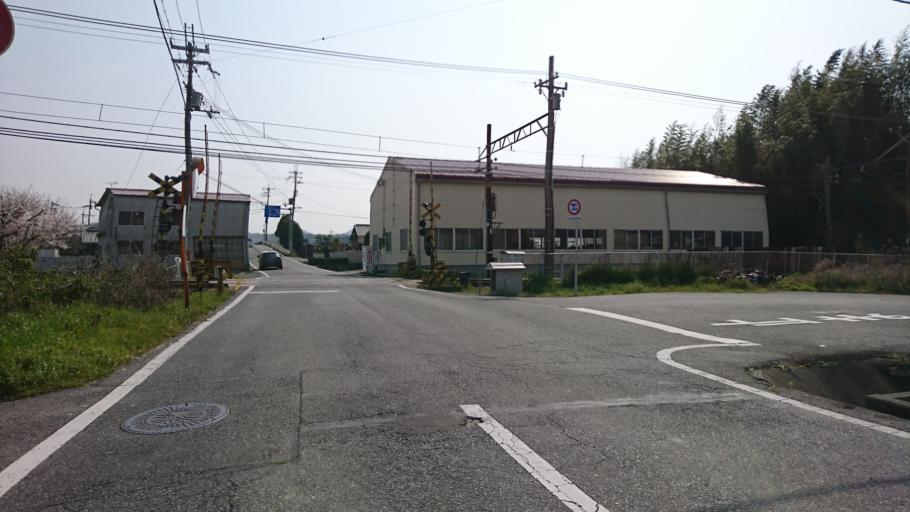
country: JP
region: Hyogo
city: Ono
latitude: 34.8534
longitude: 134.9109
